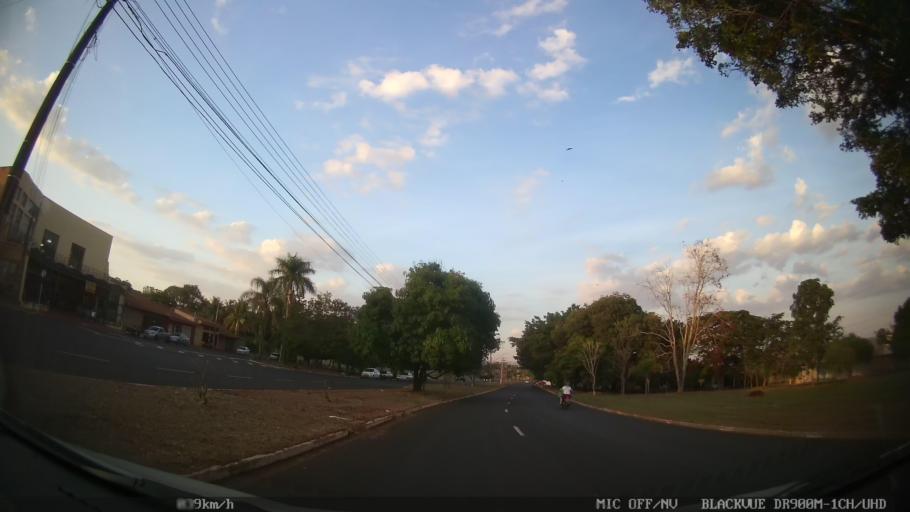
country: BR
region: Sao Paulo
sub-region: Ribeirao Preto
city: Ribeirao Preto
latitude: -21.1311
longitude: -47.8392
